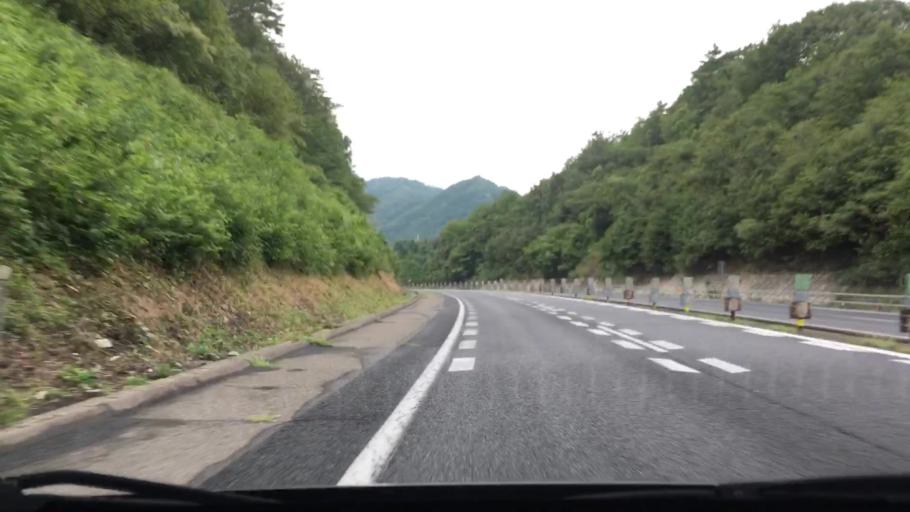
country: JP
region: Hiroshima
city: Hiroshima-shi
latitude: 34.6530
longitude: 132.5187
